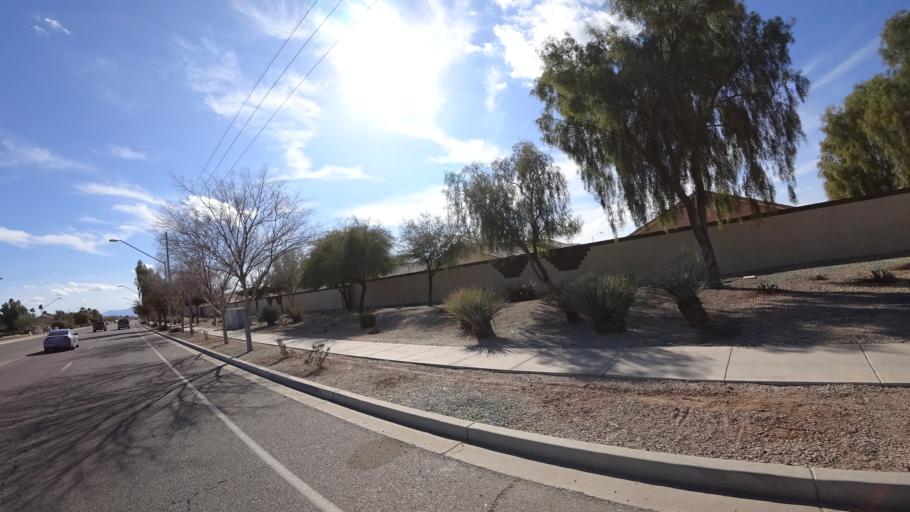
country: US
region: Arizona
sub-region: Maricopa County
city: Glendale
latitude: 33.5435
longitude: -112.2206
